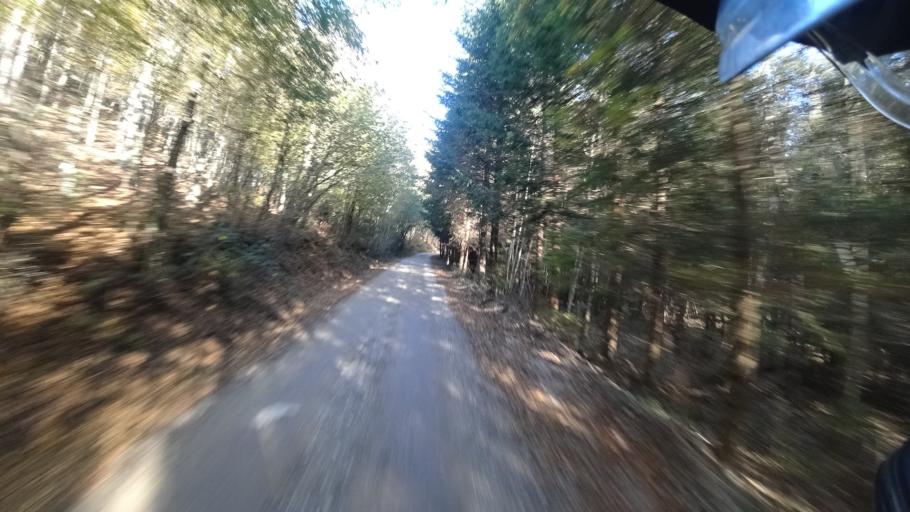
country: HR
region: Primorsko-Goranska
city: Klana
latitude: 45.5081
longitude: 14.3633
